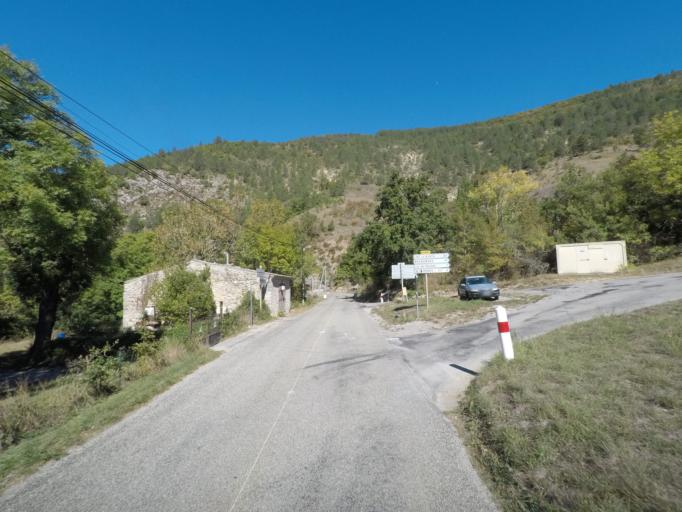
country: FR
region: Rhone-Alpes
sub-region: Departement de la Drome
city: Die
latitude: 44.6304
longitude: 5.3021
